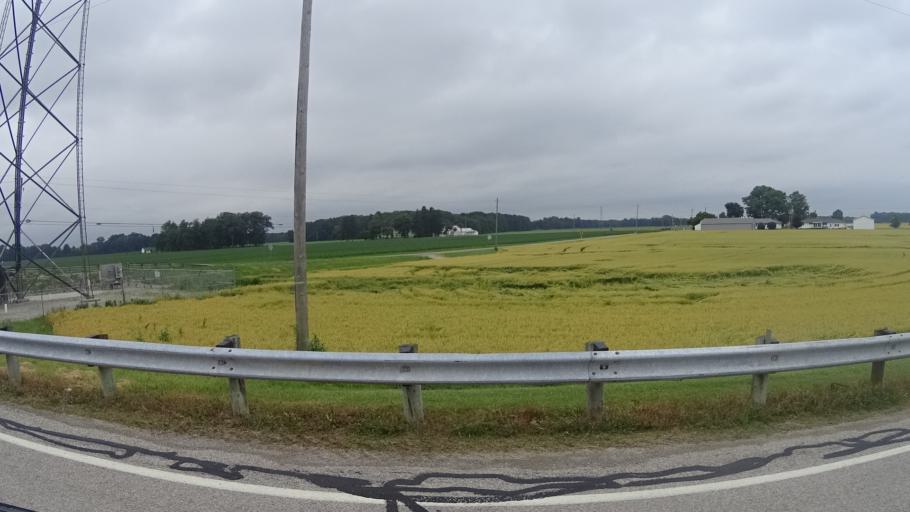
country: US
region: Ohio
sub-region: Erie County
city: Milan
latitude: 41.3264
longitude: -82.5426
